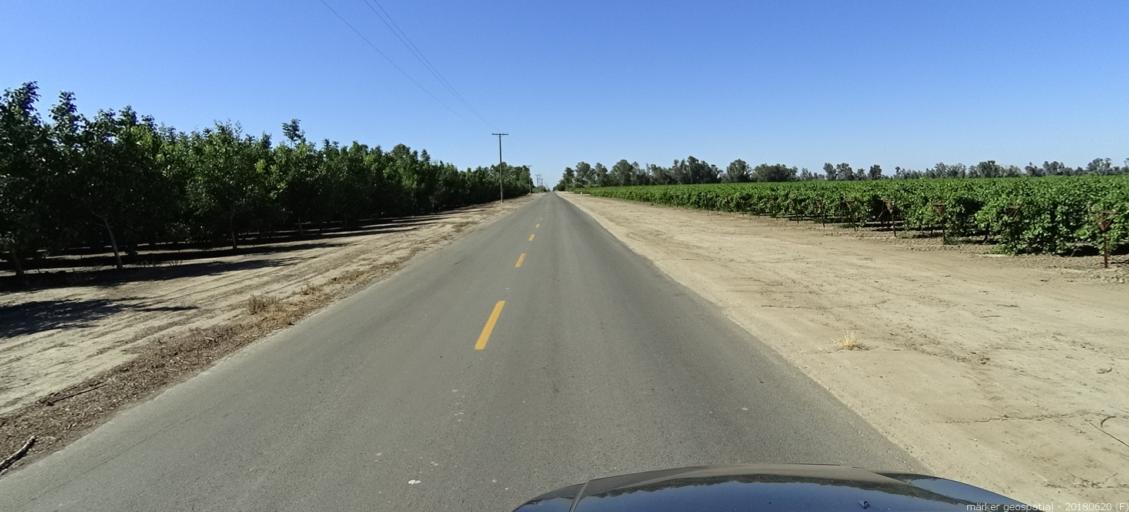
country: US
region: California
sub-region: Madera County
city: Parkwood
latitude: 36.9068
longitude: -120.0376
